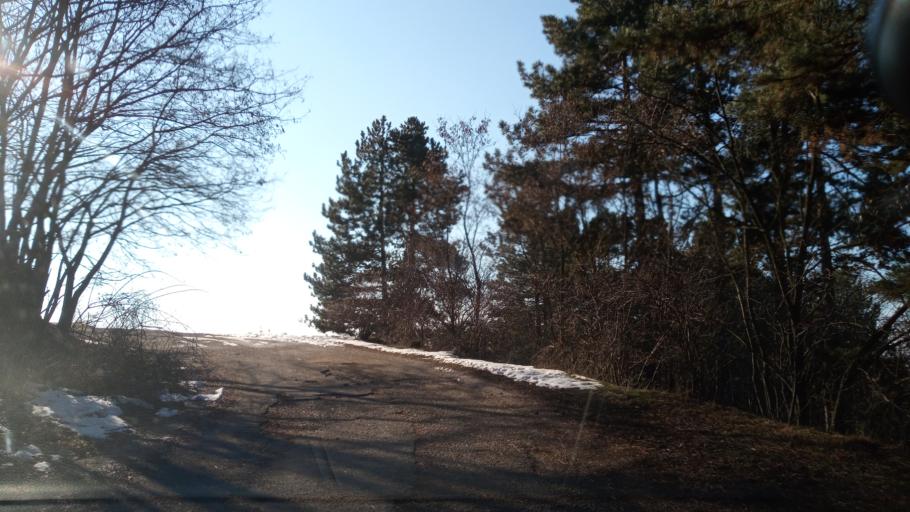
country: BG
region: Sofia-Capital
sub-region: Stolichna Obshtina
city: Bukhovo
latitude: 42.7950
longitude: 23.5314
